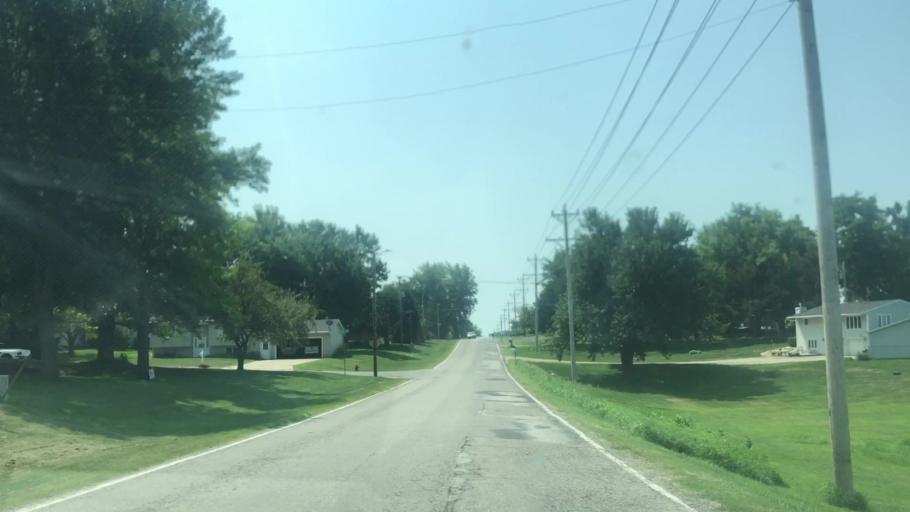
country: US
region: Iowa
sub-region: Marshall County
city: Marshalltown
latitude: 42.0428
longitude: -92.9611
